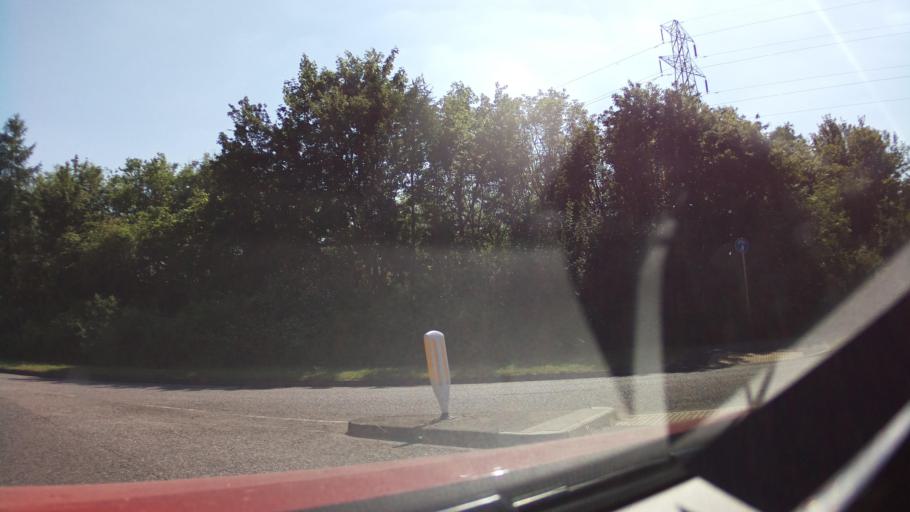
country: GB
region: England
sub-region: Hampshire
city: Andover
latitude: 51.2203
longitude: -1.4926
